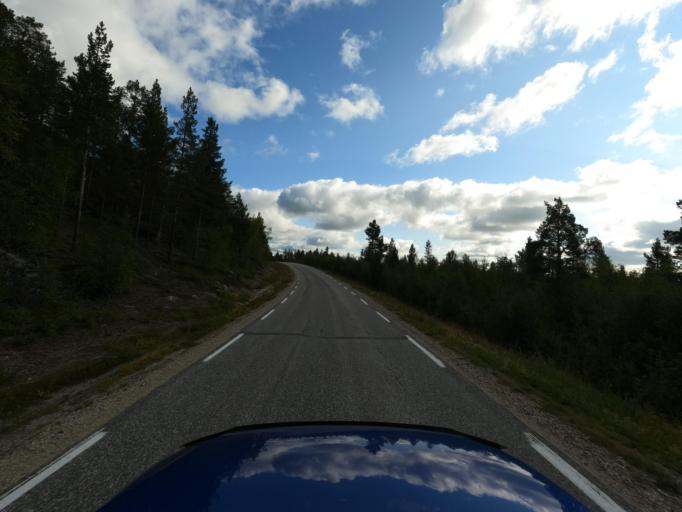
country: NO
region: Finnmark Fylke
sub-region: Karasjok
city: Karasjohka
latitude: 69.4426
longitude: 25.2547
